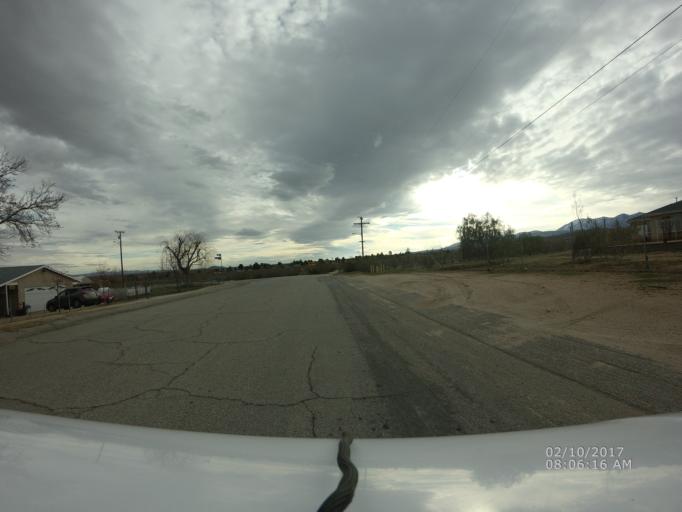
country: US
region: California
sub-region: Los Angeles County
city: Littlerock
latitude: 34.5010
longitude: -117.9102
